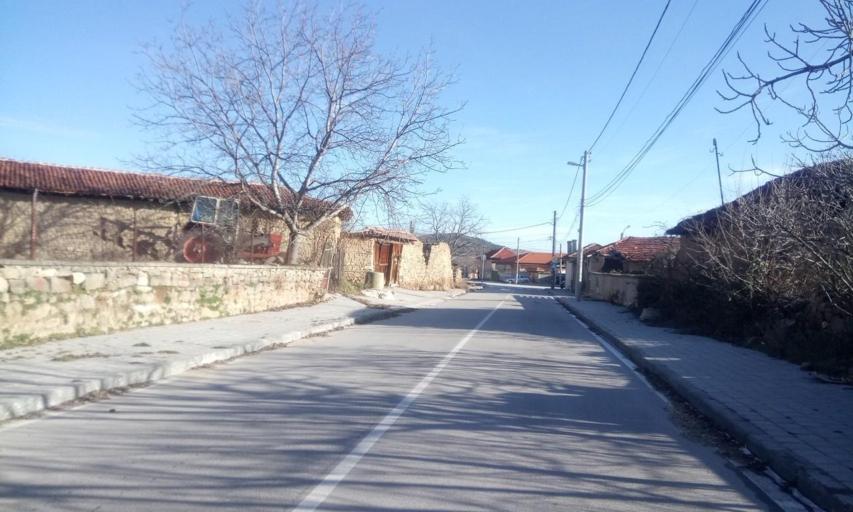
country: BG
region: Plovdiv
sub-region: Obshtina Khisarya
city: Khisarya
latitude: 42.5210
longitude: 24.7257
